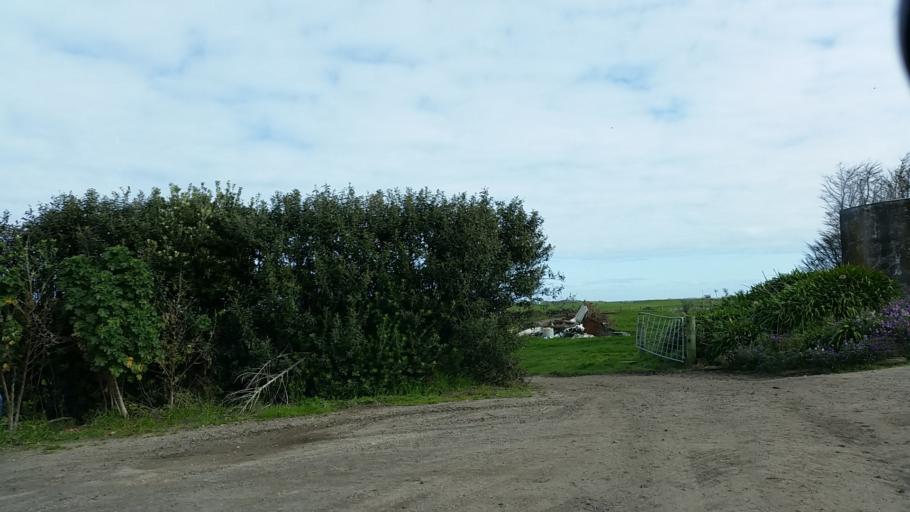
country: NZ
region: Taranaki
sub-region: South Taranaki District
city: Patea
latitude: -39.8249
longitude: 174.6490
